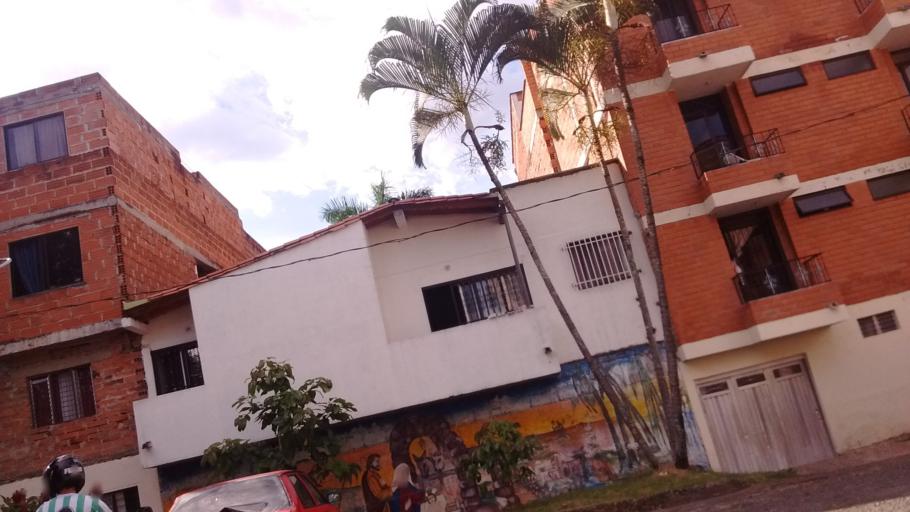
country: CO
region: Antioquia
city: Medellin
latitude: 6.2578
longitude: -75.6095
